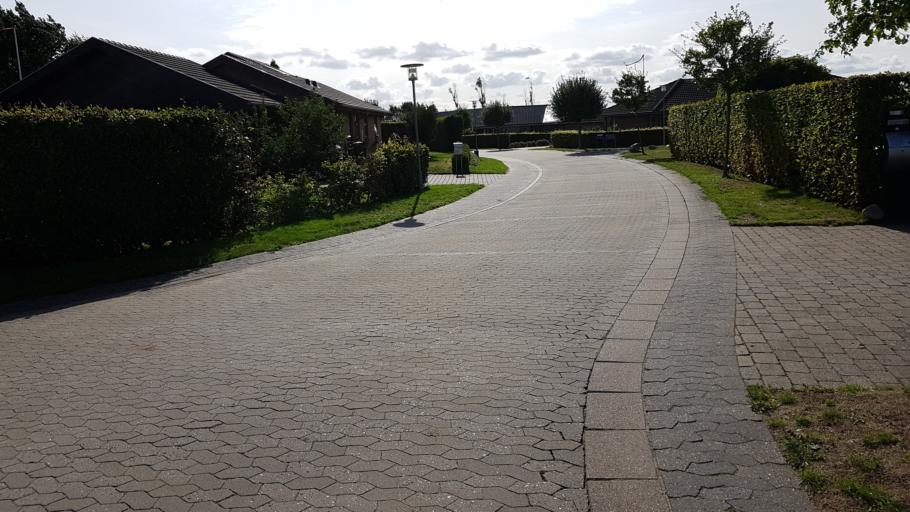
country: DK
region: Central Jutland
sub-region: Viborg Kommune
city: Viborg
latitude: 56.4705
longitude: 9.4404
